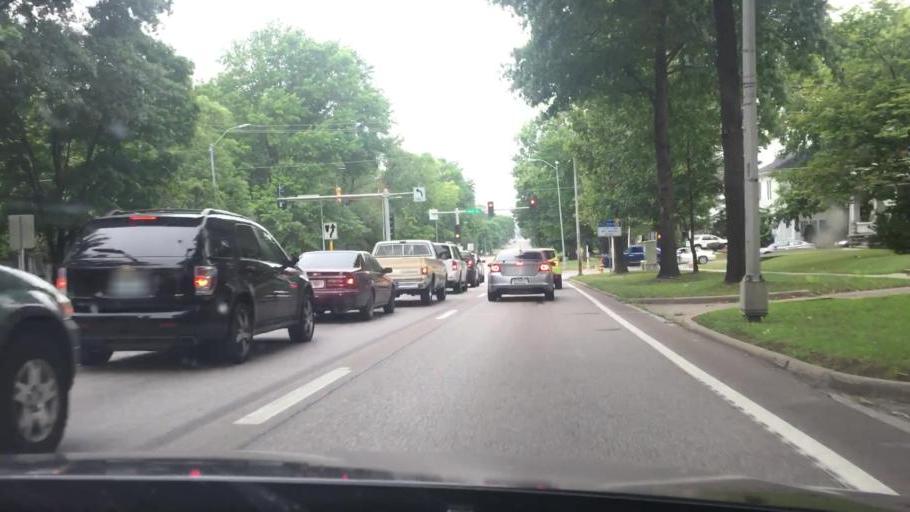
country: US
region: Missouri
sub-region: Pettis County
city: Sedalia
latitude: 38.7046
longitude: -93.2357
